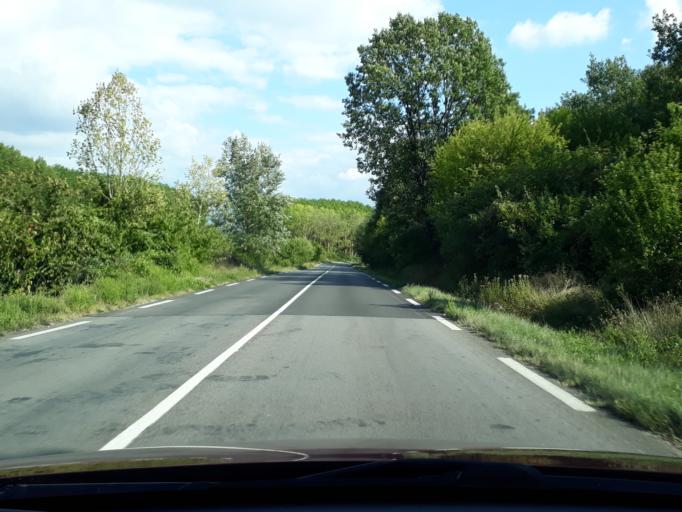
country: FR
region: Rhone-Alpes
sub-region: Departement de la Loire
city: Chavanay
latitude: 45.3961
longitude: 4.7406
